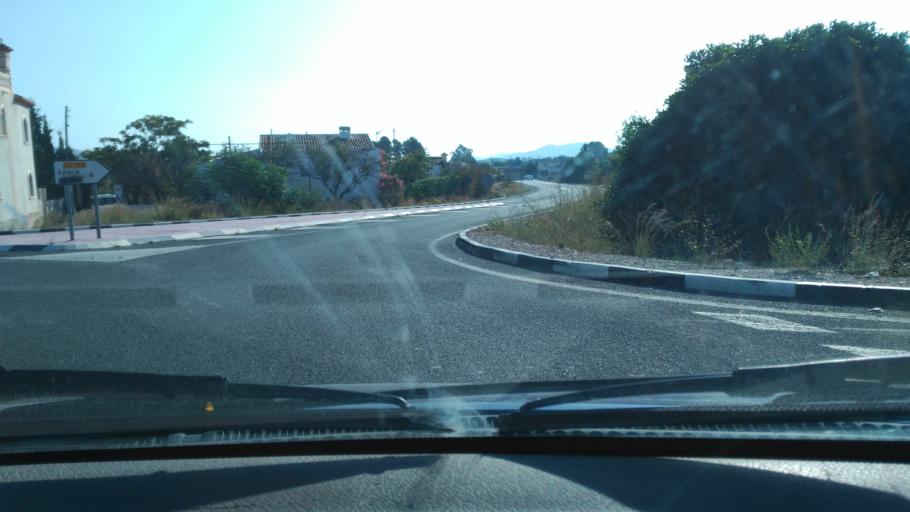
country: ES
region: Valencia
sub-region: Provincia de Alicante
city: Gata de Gorgos
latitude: 38.7846
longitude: 0.0848
